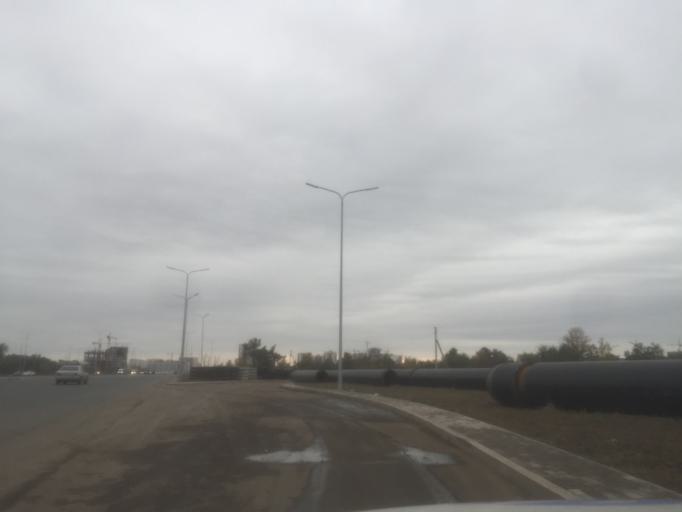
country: KZ
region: Astana Qalasy
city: Astana
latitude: 51.1593
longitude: 71.3726
